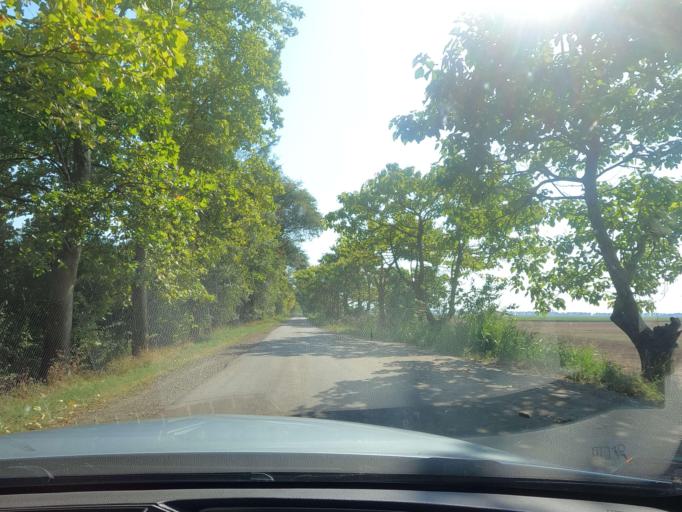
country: RS
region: Autonomna Pokrajina Vojvodina
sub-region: Juznobacki Okrug
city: Becej
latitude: 45.6679
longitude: 19.9109
